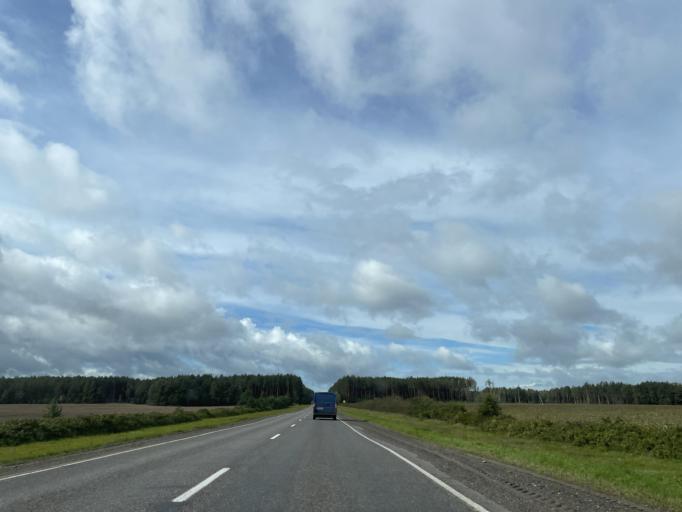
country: BY
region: Brest
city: Kosava
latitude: 52.7356
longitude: 25.2439
